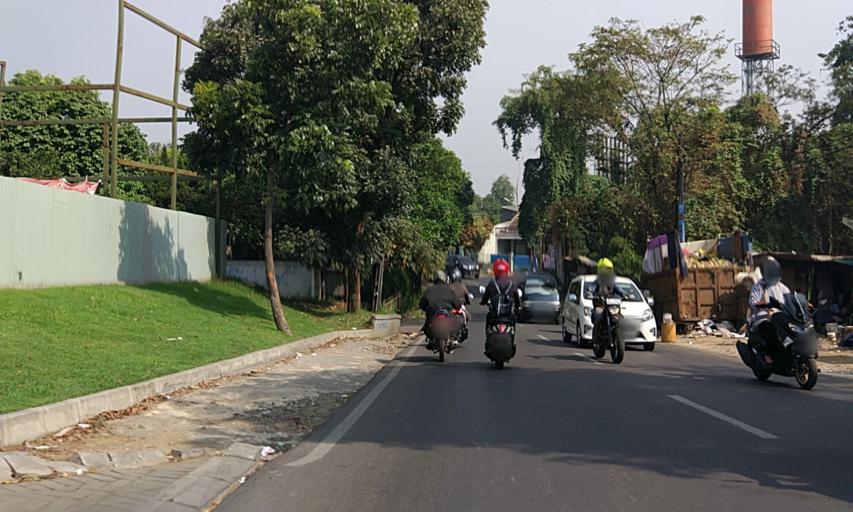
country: ID
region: West Java
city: Cimahi
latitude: -6.8890
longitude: 107.5655
